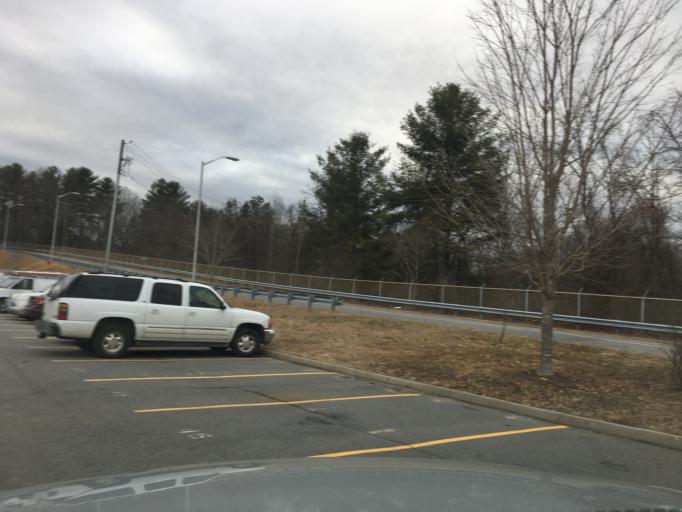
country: US
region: North Carolina
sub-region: Buncombe County
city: Woodfin
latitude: 35.6075
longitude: -82.5844
